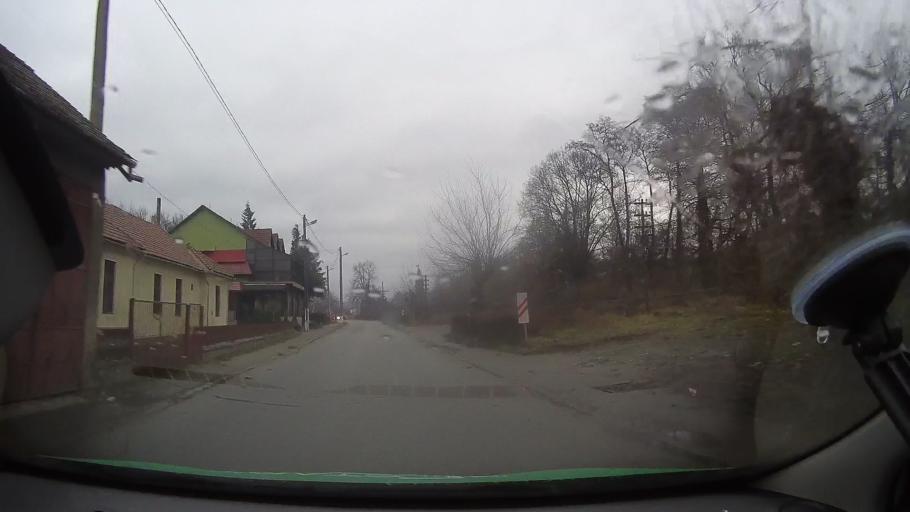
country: RO
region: Hunedoara
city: Vata de Jos
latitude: 46.1793
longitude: 22.6006
